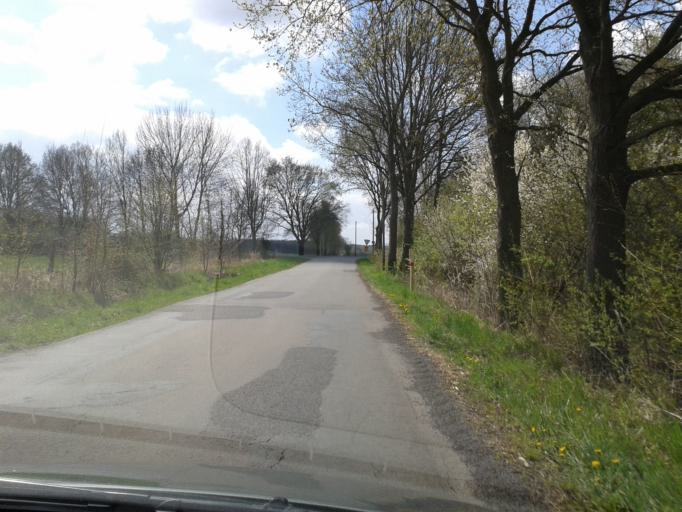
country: DE
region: Lower Saxony
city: Wustrow
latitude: 52.9239
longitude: 11.1076
